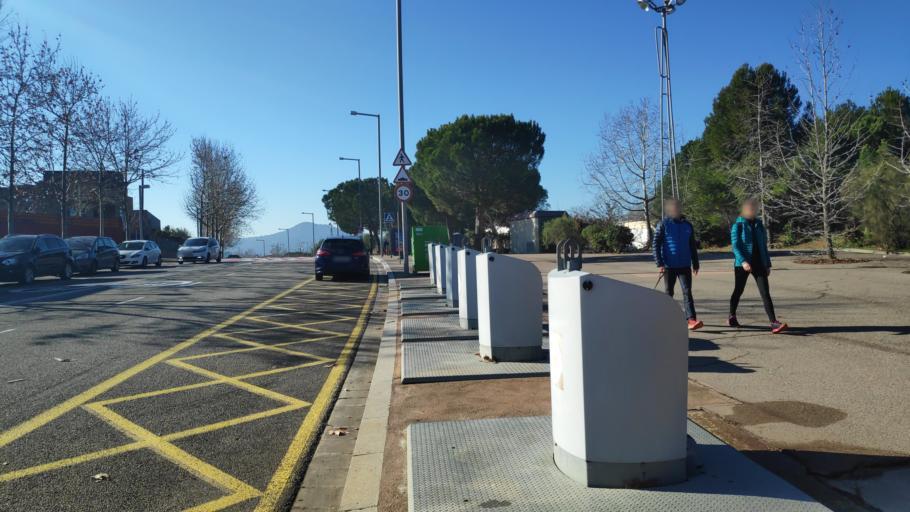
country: ES
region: Catalonia
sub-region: Provincia de Barcelona
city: Sant Cugat del Valles
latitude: 41.4737
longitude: 2.0626
